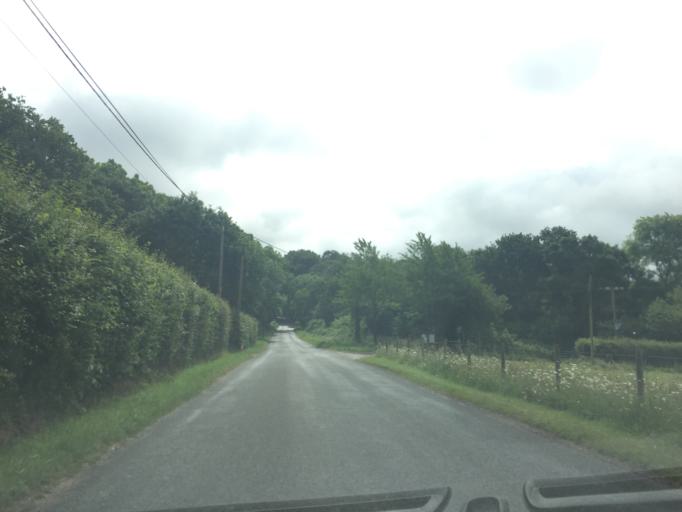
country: GB
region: England
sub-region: Dorset
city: Bovington Camp
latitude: 50.7199
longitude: -2.2894
